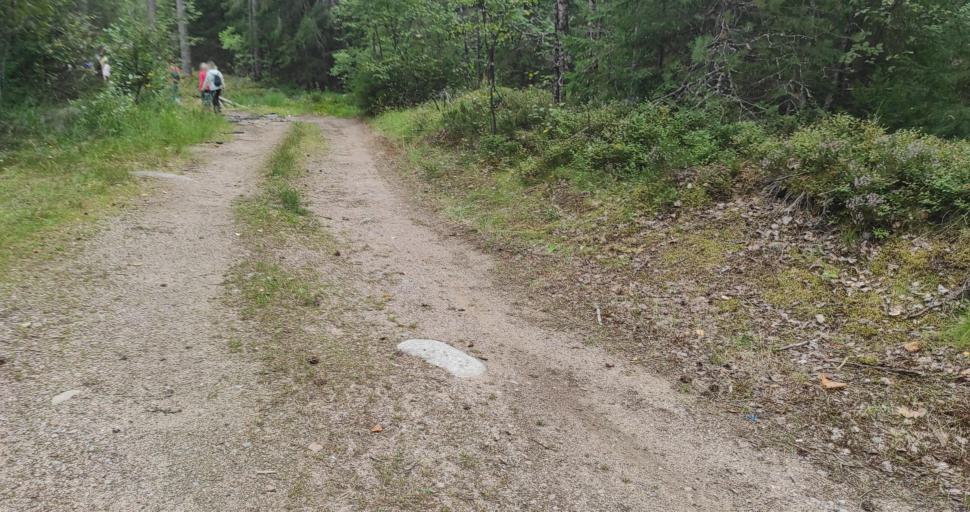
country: RU
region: Leningrad
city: Veshchevo
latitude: 60.6865
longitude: 29.2501
